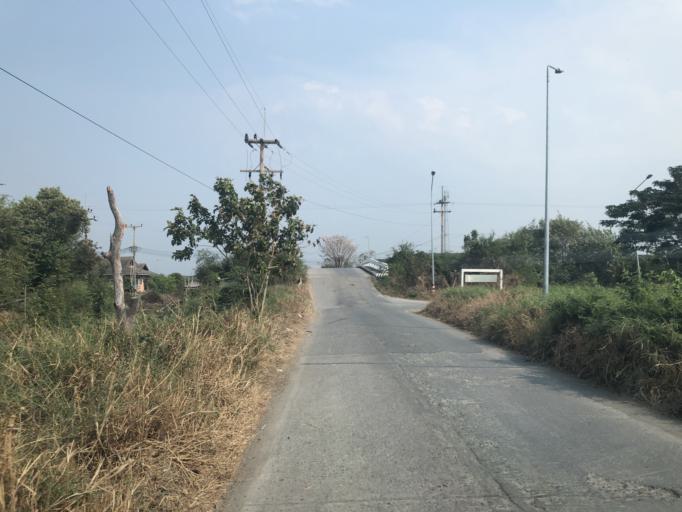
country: TH
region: Chachoengsao
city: Bang Pakong
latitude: 13.5118
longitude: 100.9255
